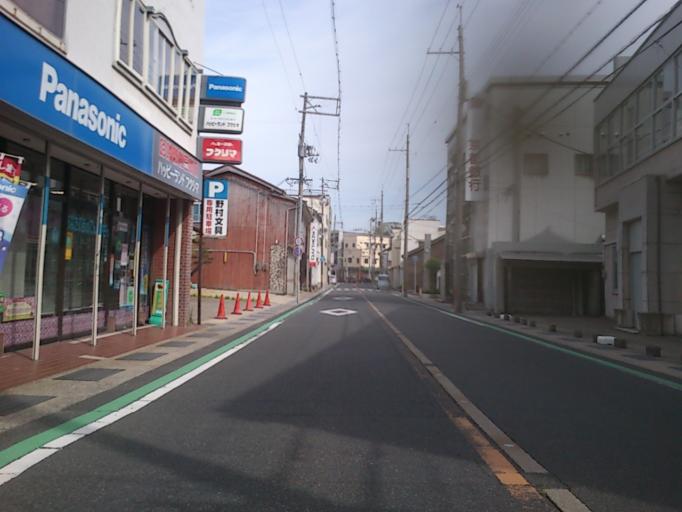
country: JP
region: Kyoto
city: Miyazu
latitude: 35.6819
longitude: 135.0274
